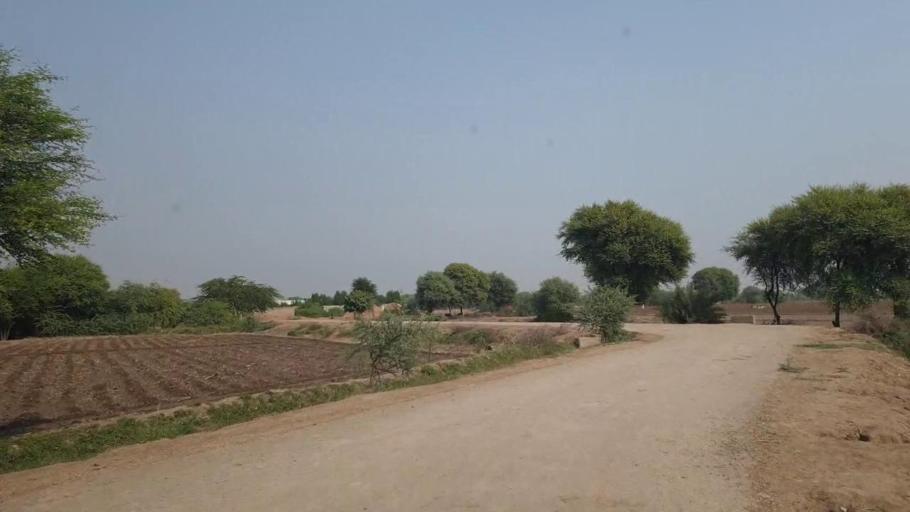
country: PK
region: Sindh
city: Matli
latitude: 25.1511
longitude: 68.7016
